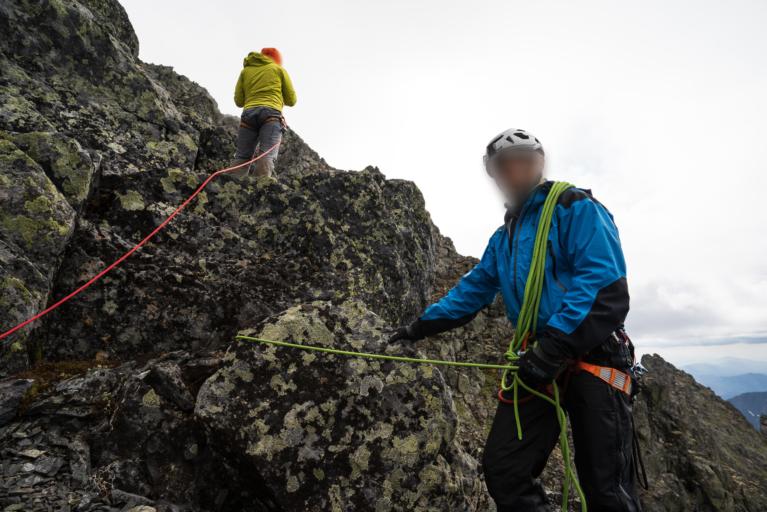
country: RU
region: Komi Republic
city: Synya
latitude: 64.7769
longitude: 58.8851
